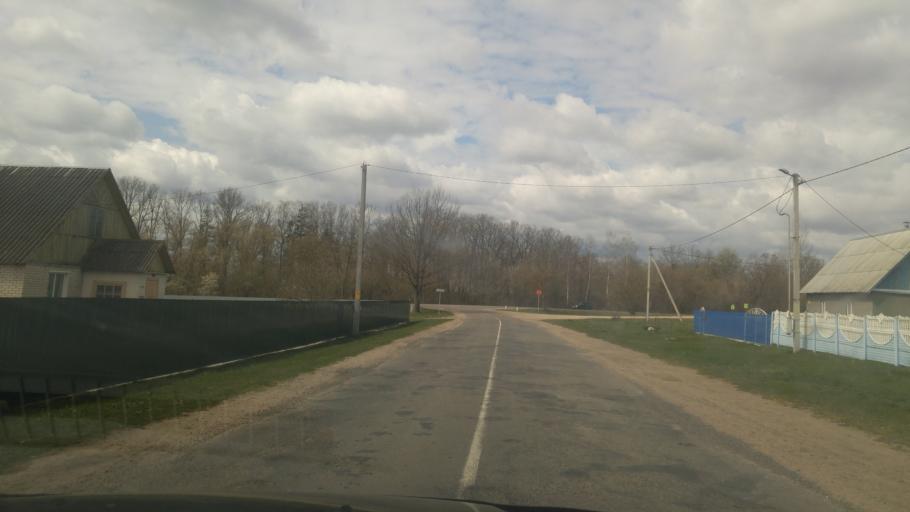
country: BY
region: Minsk
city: Pukhavichy
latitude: 53.4160
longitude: 28.2612
